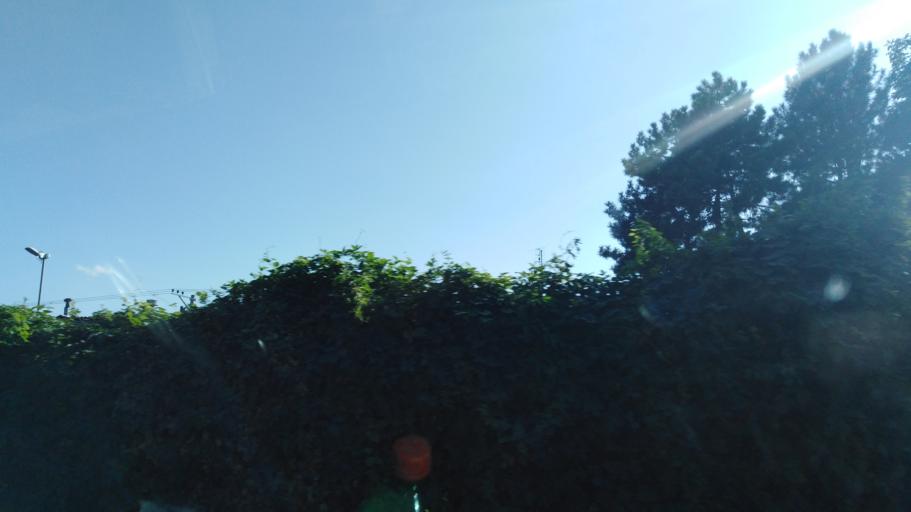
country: RU
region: Stavropol'skiy
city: Svobody
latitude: 44.0391
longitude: 43.0387
